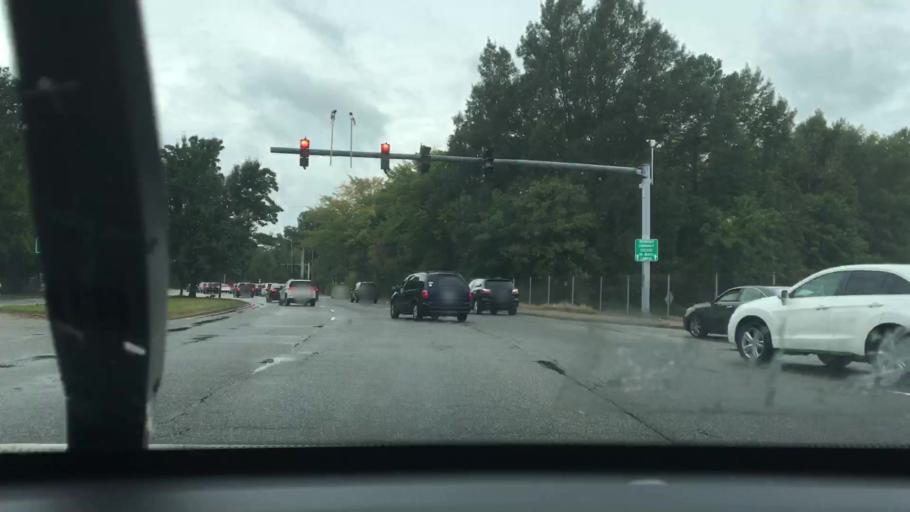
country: US
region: Virginia
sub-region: City of Virginia Beach
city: Virginia Beach
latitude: 36.8350
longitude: -76.0670
